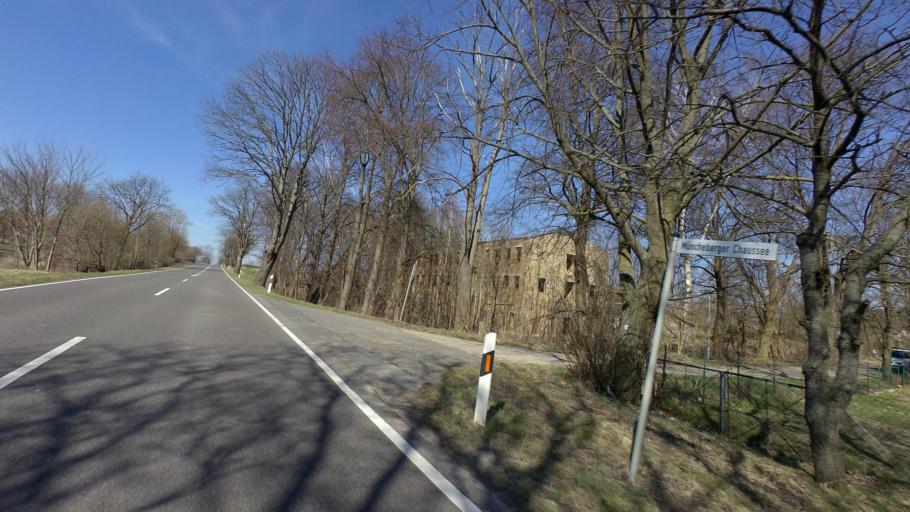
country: DE
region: Brandenburg
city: Protzel
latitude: 52.5961
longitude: 14.0259
